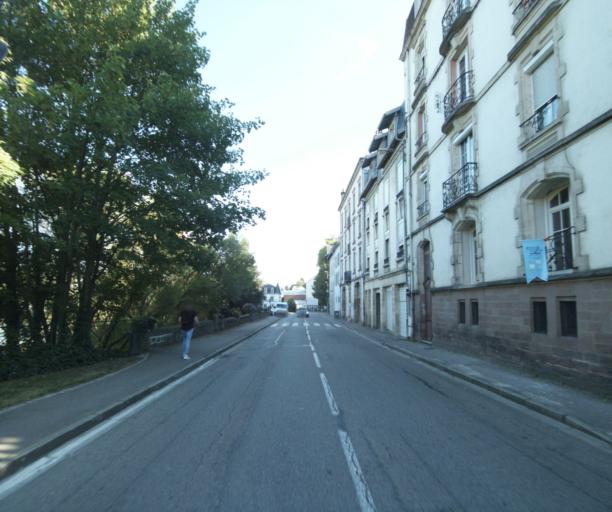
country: FR
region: Lorraine
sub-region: Departement des Vosges
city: Chantraine
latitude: 48.1687
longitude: 6.4450
